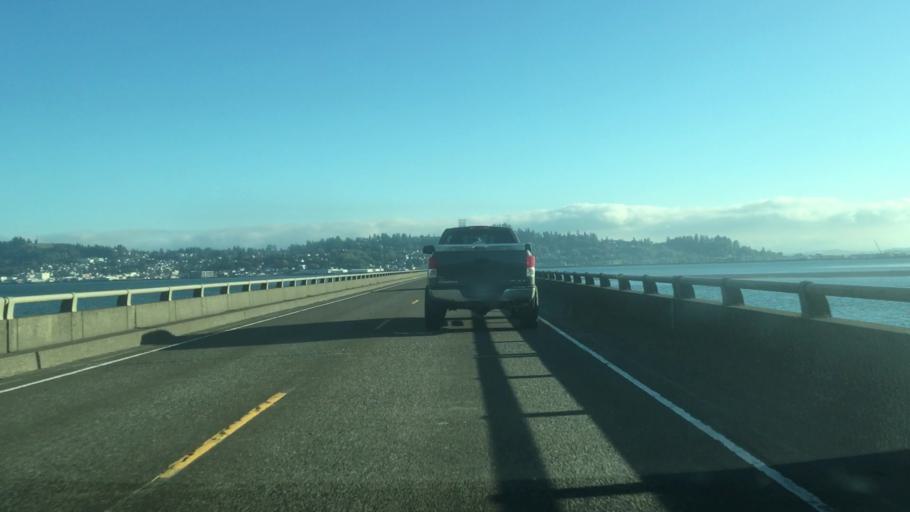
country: US
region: Oregon
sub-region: Clatsop County
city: Astoria
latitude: 46.2111
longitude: -123.8599
